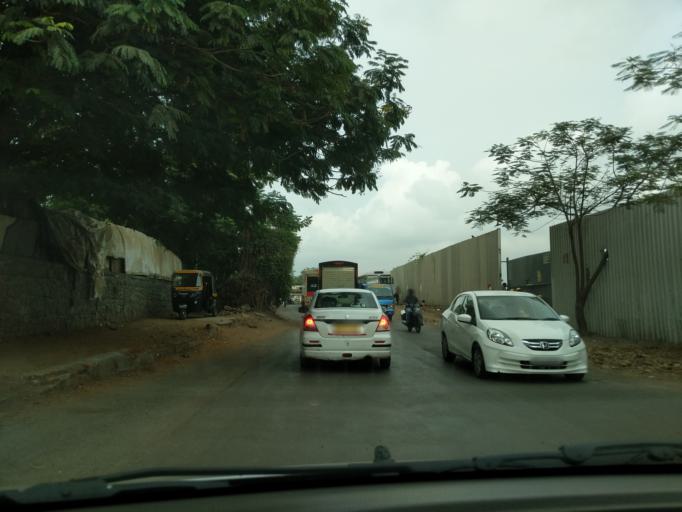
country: IN
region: Maharashtra
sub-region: Mumbai Suburban
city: Mumbai
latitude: 19.1004
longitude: 72.8780
